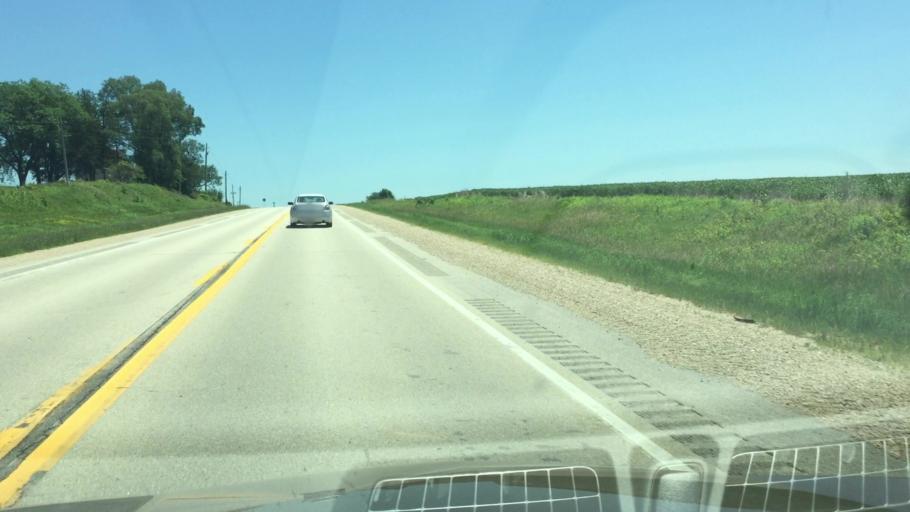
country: US
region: Iowa
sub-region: Jackson County
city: Maquoketa
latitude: 42.0718
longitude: -90.7980
